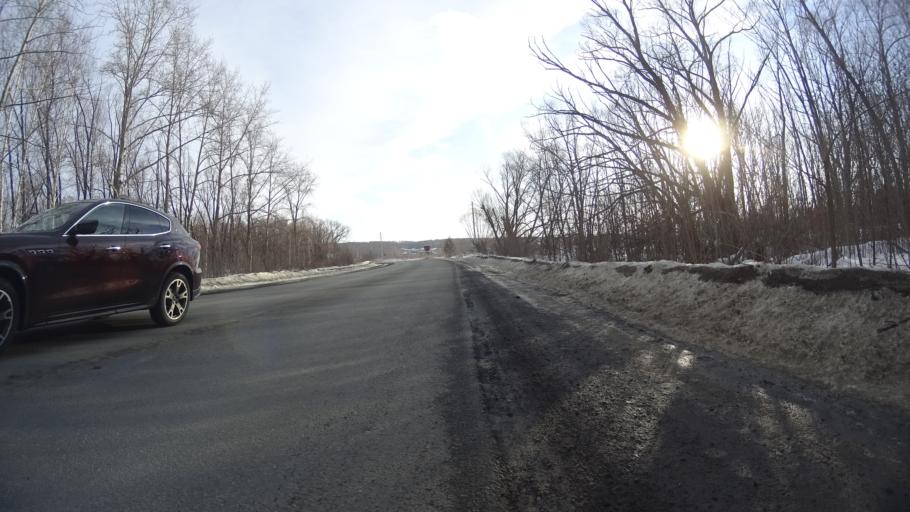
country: RU
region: Chelyabinsk
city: Sargazy
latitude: 55.1413
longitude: 61.2823
